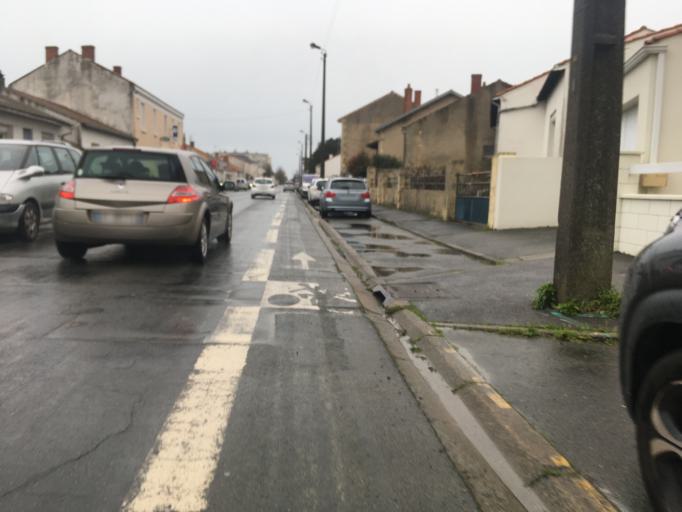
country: FR
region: Poitou-Charentes
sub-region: Departement de la Charente-Maritime
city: La Rochelle
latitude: 46.1641
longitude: -1.2053
